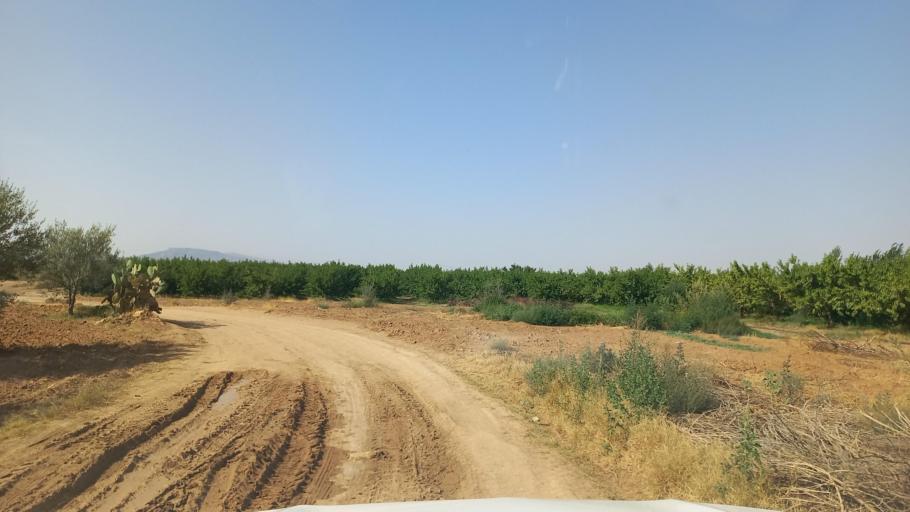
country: TN
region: Al Qasrayn
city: Kasserine
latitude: 35.2527
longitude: 9.0438
